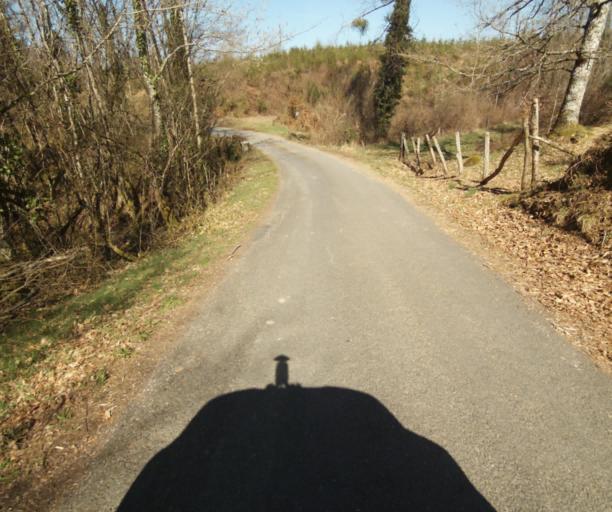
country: FR
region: Limousin
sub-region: Departement de la Correze
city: Saint-Mexant
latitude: 45.3124
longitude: 1.5974
